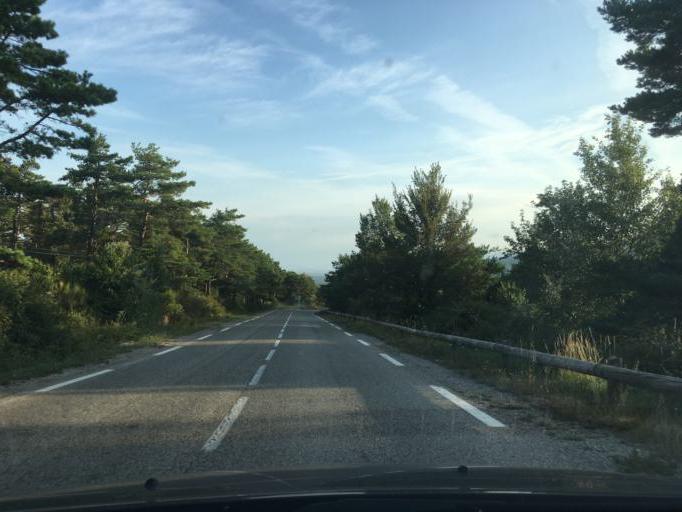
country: FR
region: Provence-Alpes-Cote d'Azur
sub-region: Departement du Var
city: Aups
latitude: 43.6648
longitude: 6.2273
